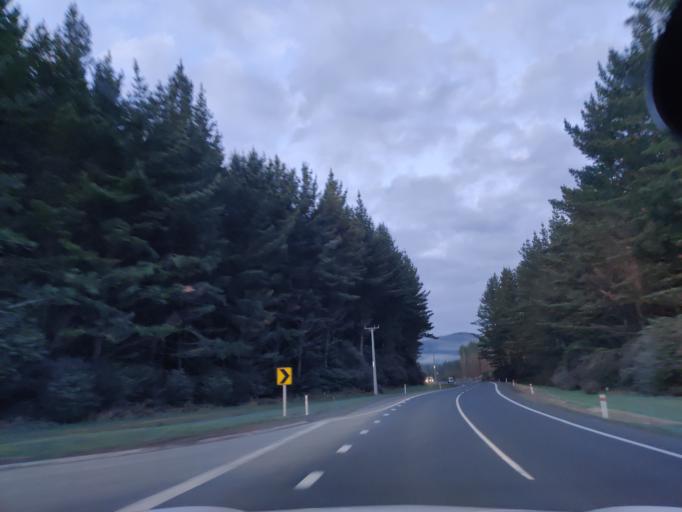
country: NZ
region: Waikato
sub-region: South Waikato District
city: Tokoroa
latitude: -38.3666
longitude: 176.0028
